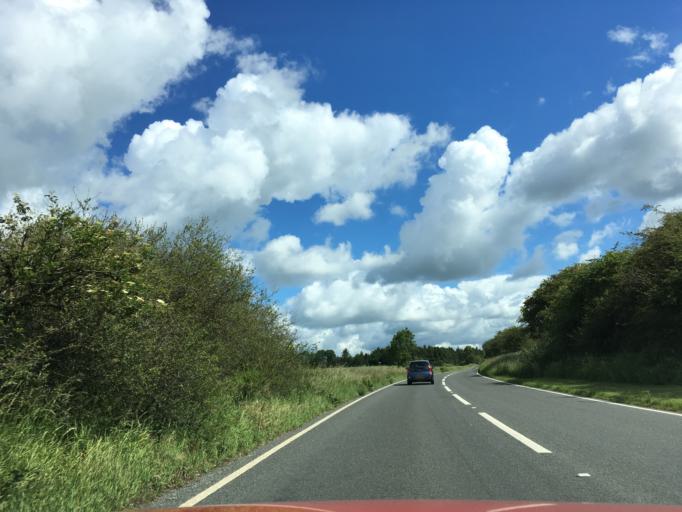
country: GB
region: England
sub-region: Oxfordshire
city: Burford
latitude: 51.7939
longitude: -1.6441
